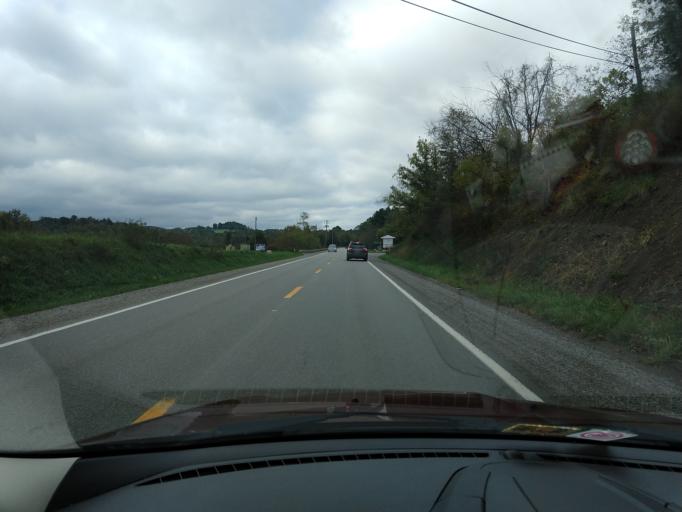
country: US
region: West Virginia
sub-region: Barbour County
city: Belington
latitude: 39.0328
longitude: -79.9454
